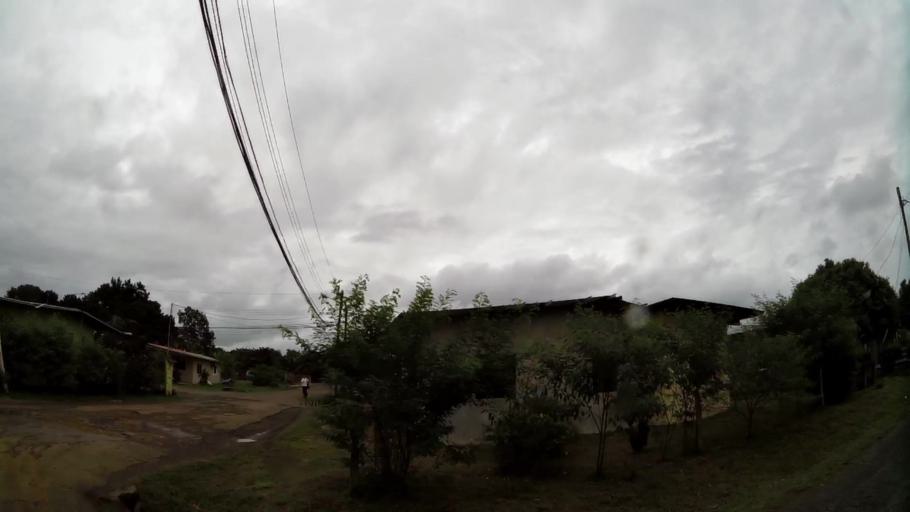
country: PA
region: Chiriqui
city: David
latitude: 8.3995
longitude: -82.4540
